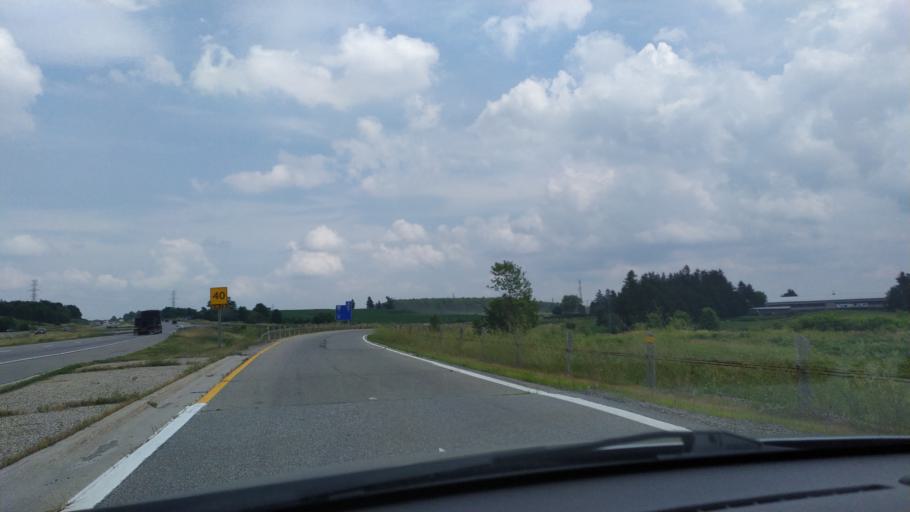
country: CA
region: Ontario
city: Kitchener
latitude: 43.4088
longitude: -80.5516
